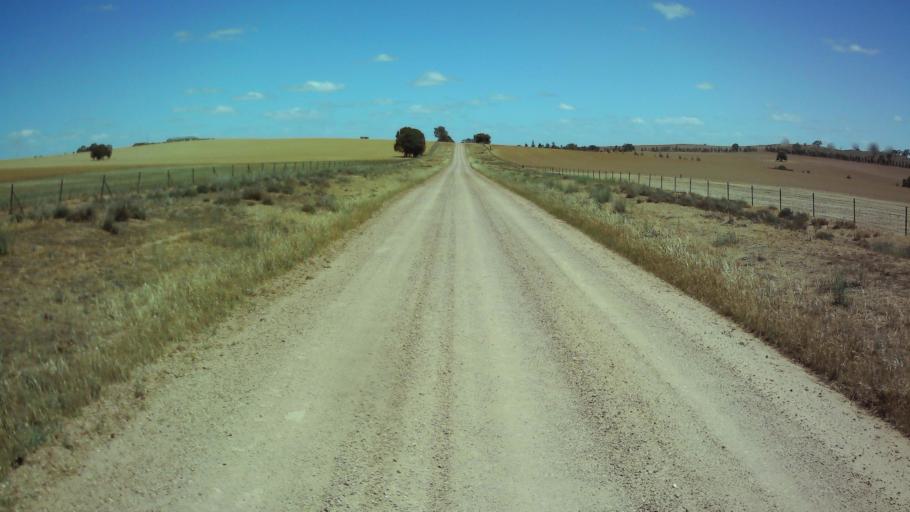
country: AU
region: New South Wales
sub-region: Weddin
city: Grenfell
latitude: -33.9442
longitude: 148.3298
